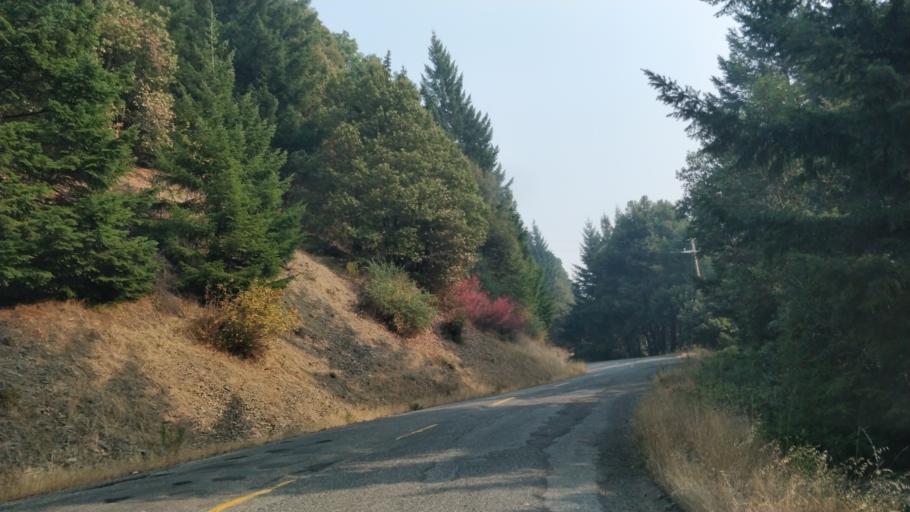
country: US
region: California
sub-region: Humboldt County
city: Rio Dell
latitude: 40.2782
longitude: -124.0747
